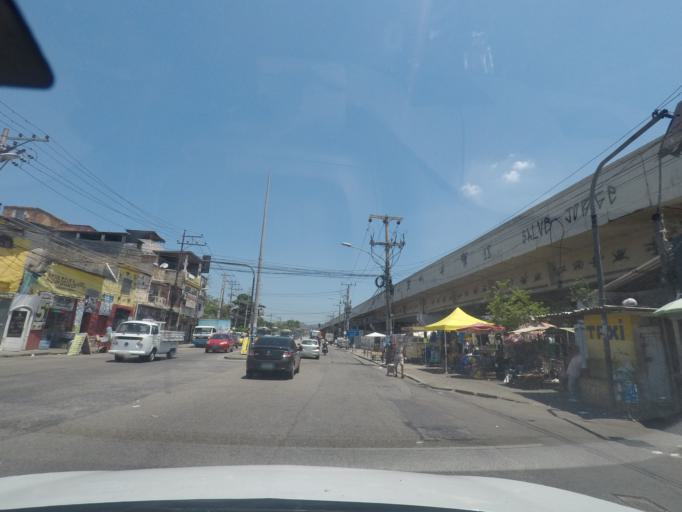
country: BR
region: Rio de Janeiro
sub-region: Rio De Janeiro
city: Rio de Janeiro
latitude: -22.8831
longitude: -43.2544
